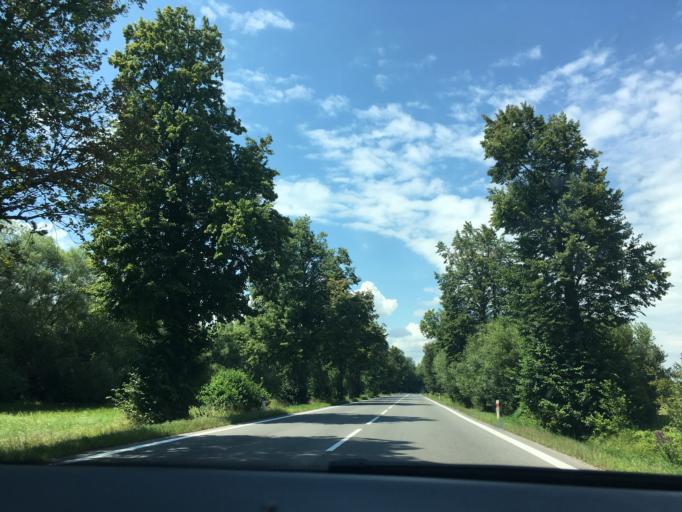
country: SK
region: Presovsky
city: Vranov nad Topl'ou
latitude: 48.8606
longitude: 21.7187
